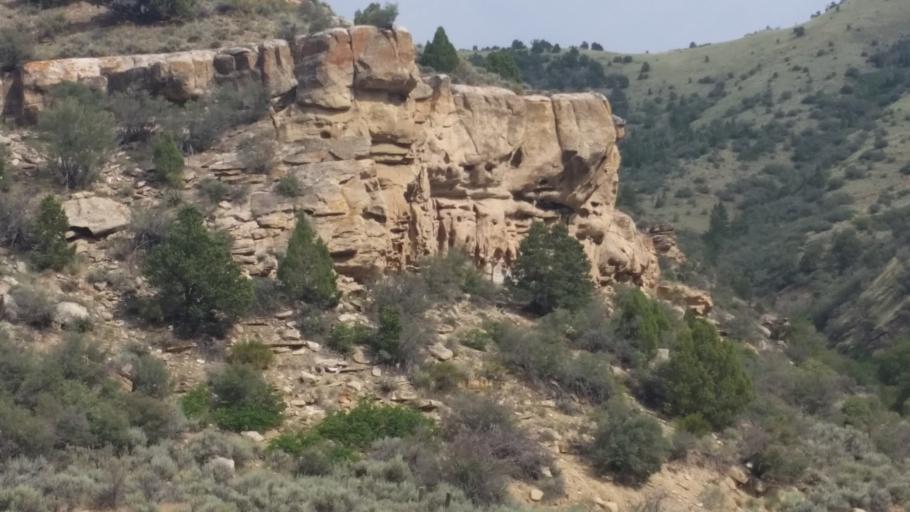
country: US
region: Utah
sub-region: Carbon County
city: Helper
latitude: 39.7290
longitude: -110.8549
